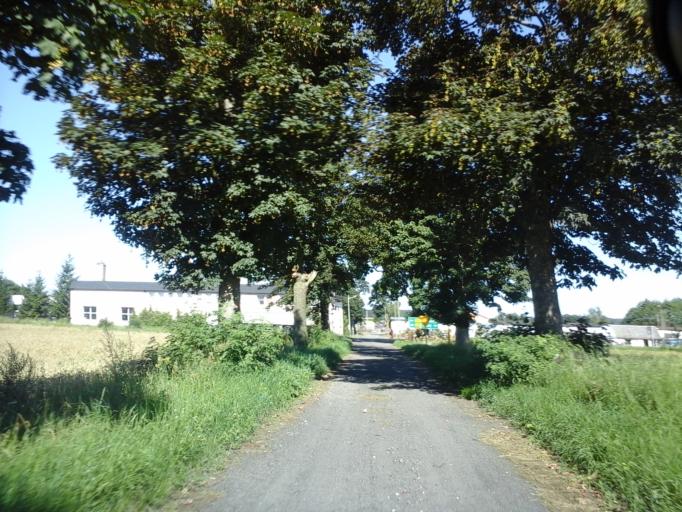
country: PL
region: West Pomeranian Voivodeship
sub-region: Powiat choszczenski
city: Choszczno
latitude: 53.2017
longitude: 15.4524
